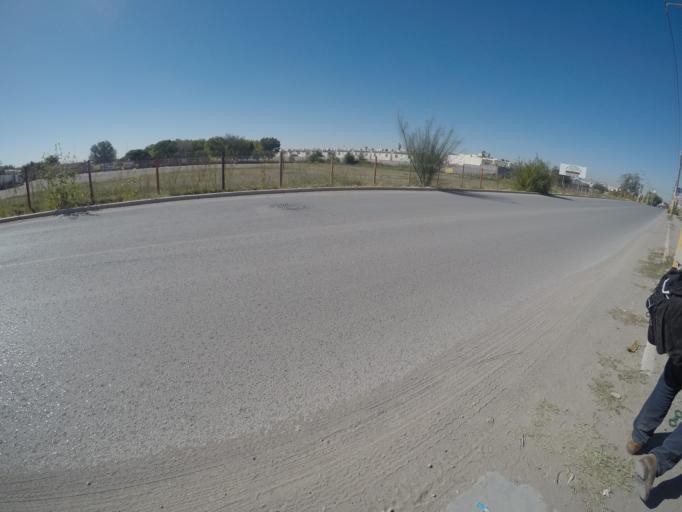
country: US
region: Texas
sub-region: El Paso County
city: Socorro
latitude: 31.6907
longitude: -106.3569
